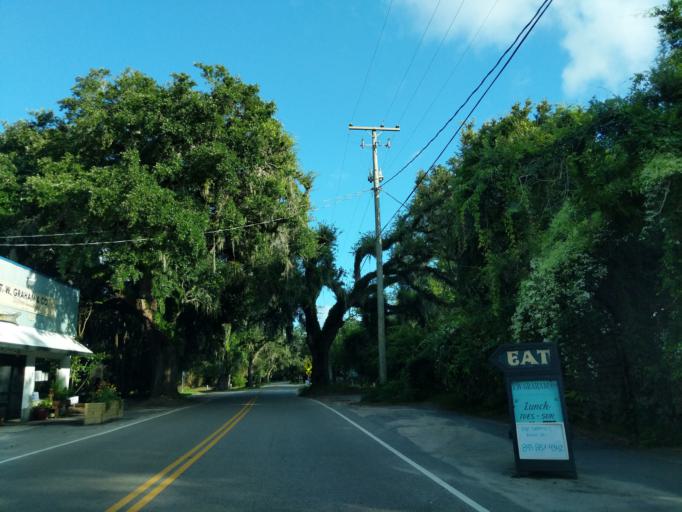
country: US
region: South Carolina
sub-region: Charleston County
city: Awendaw
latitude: 33.0900
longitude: -79.4626
